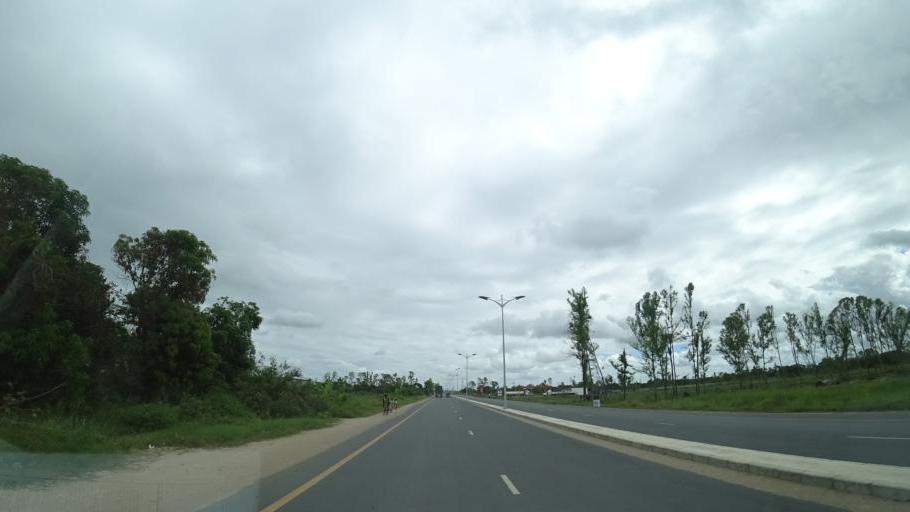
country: MZ
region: Sofala
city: Dondo
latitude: -19.7029
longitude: 34.7886
